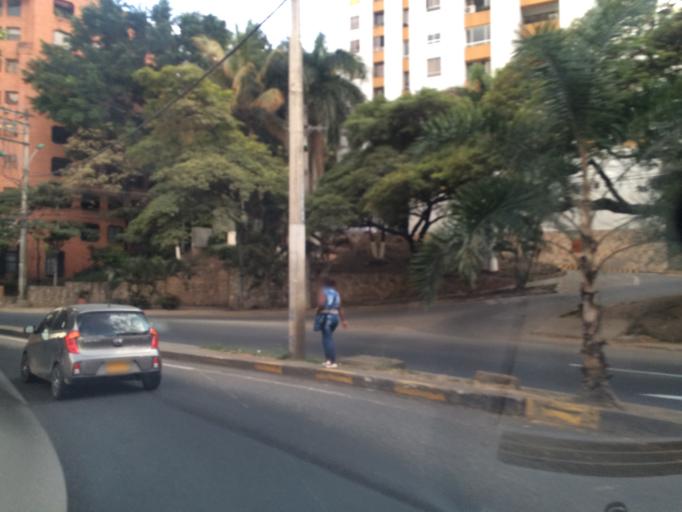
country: CO
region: Valle del Cauca
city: Cali
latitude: 3.4542
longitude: -76.5465
